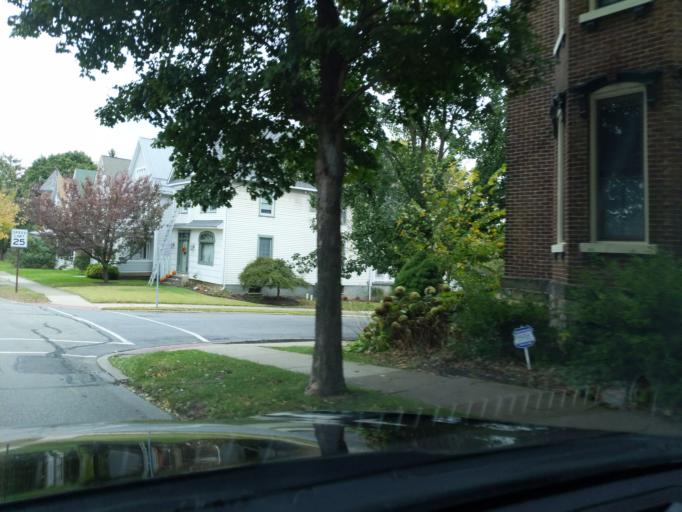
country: US
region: Pennsylvania
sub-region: Blair County
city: Hollidaysburg
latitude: 40.4325
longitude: -78.3910
